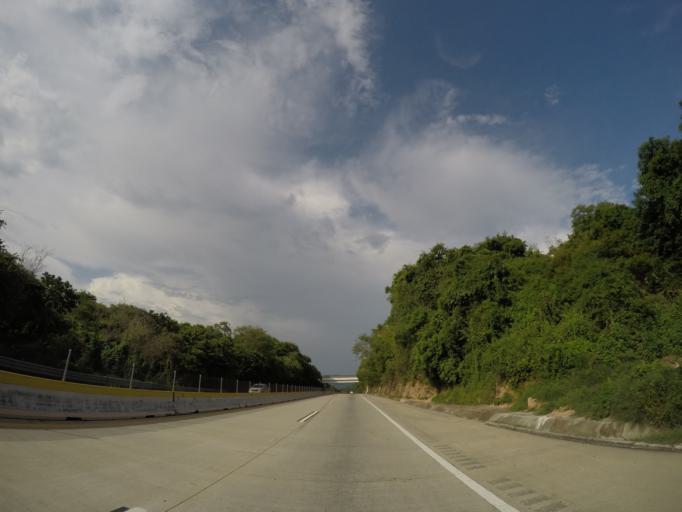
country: MX
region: Guerrero
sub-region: Acapulco de Juarez
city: Kilometro 30
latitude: 16.9740
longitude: -99.7240
